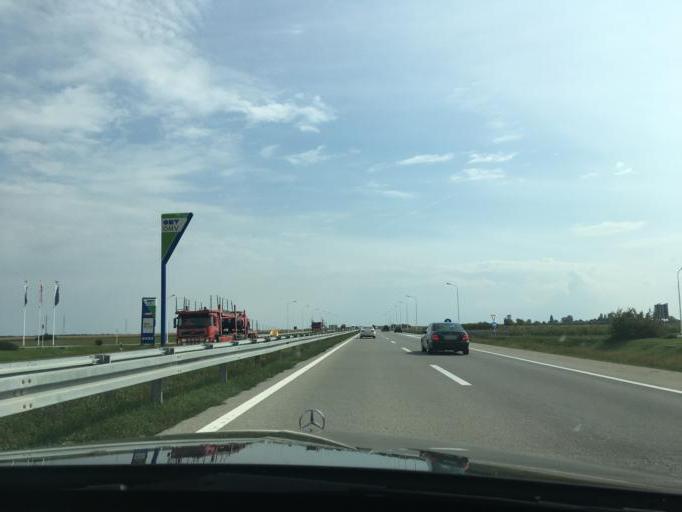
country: RS
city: Ravnje
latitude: 45.0360
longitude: 19.4493
